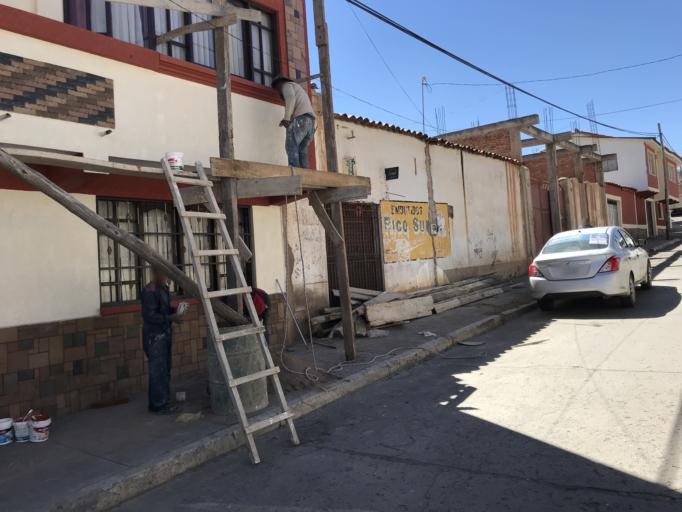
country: BO
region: Chuquisaca
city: Sucre
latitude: -19.0395
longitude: -65.2513
